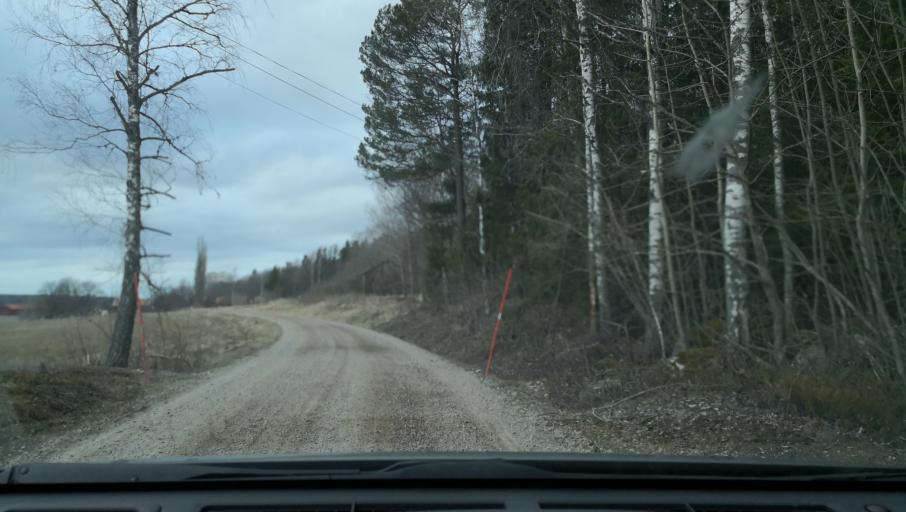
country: SE
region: Vaestmanland
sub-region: Kopings Kommun
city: Koping
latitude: 59.5313
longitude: 15.9046
